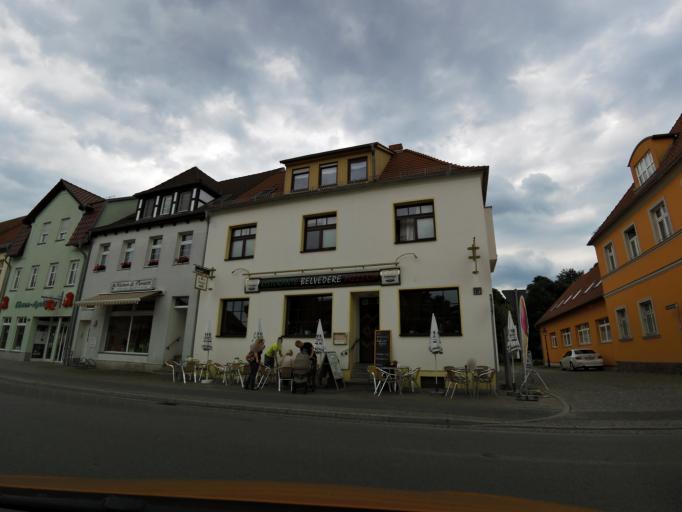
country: DE
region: Brandenburg
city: Baruth
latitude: 52.0495
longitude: 13.5042
